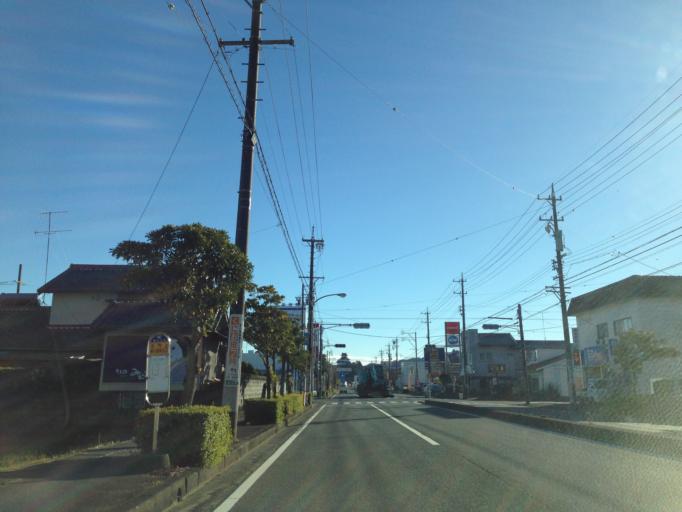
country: JP
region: Shizuoka
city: Kakegawa
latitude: 34.7829
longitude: 138.0133
